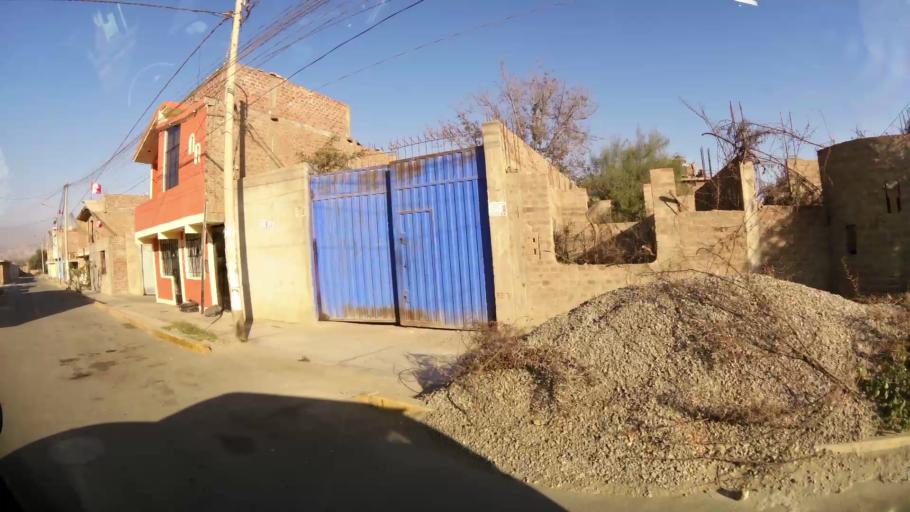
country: PE
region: Ica
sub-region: Provincia de Ica
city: Ica
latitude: -14.0683
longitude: -75.7178
